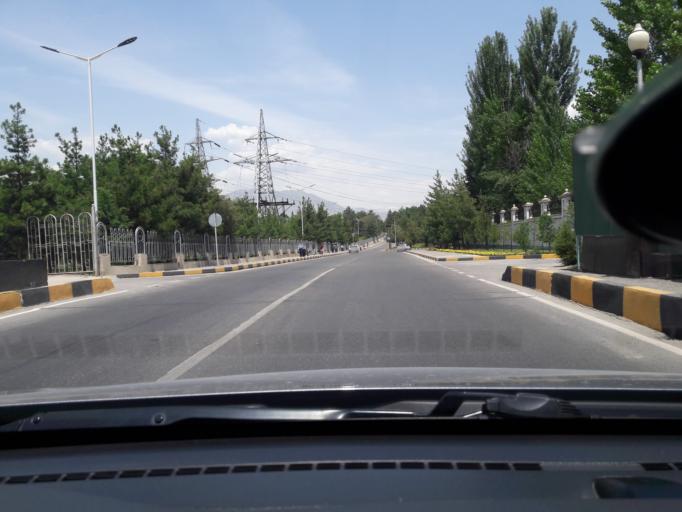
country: TJ
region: Dushanbe
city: Dushanbe
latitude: 38.5803
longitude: 68.7733
